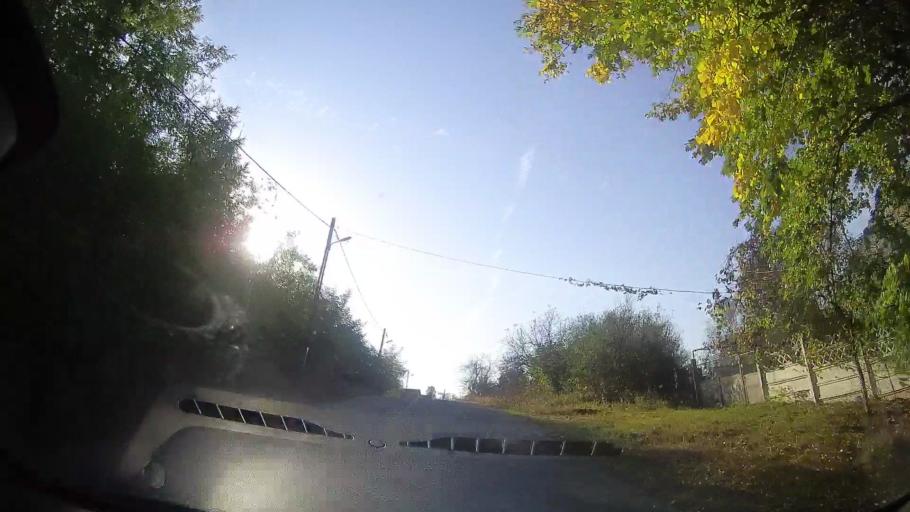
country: RO
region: Timis
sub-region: Comuna Bogda
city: Bogda
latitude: 45.9646
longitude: 21.6116
